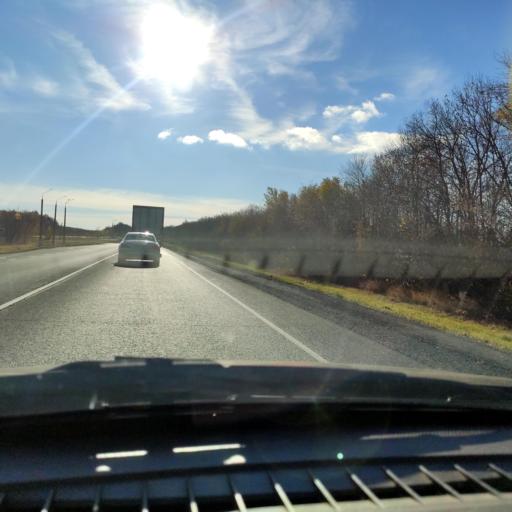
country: RU
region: Samara
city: Zhigulevsk
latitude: 53.3172
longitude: 49.3649
